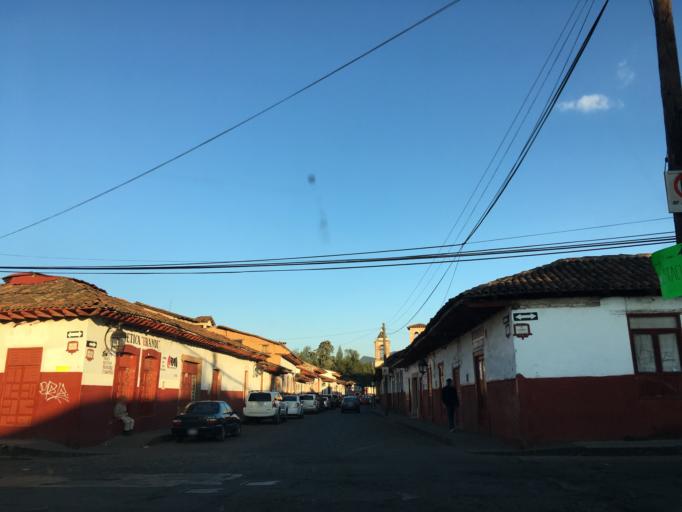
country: MX
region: Michoacan
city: Patzcuaro
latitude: 19.5135
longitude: -101.6143
